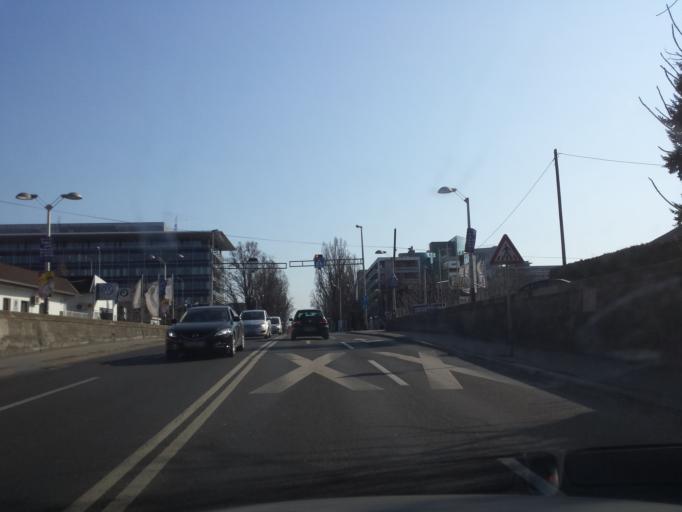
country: HR
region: Grad Zagreb
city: Zagreb - Centar
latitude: 45.8036
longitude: 15.9742
